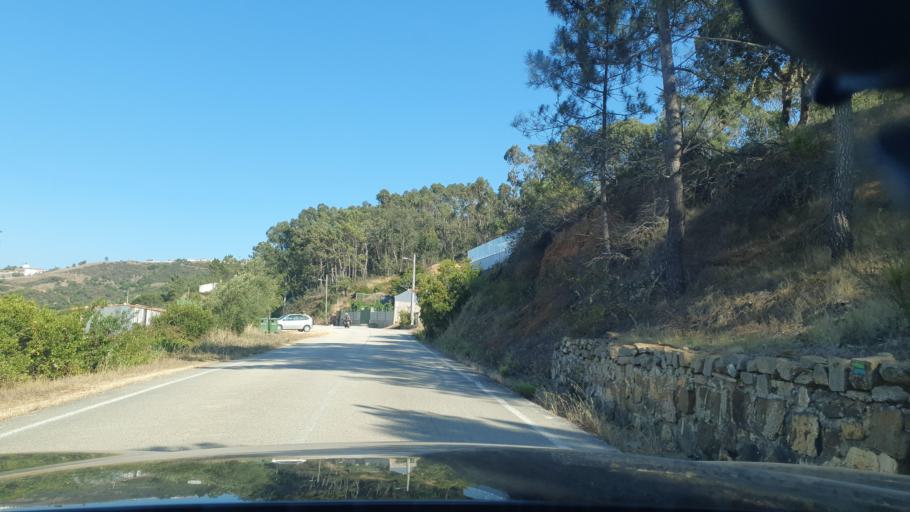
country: PT
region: Beja
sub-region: Odemira
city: Sao Teotonio
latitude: 37.4333
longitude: -8.7846
